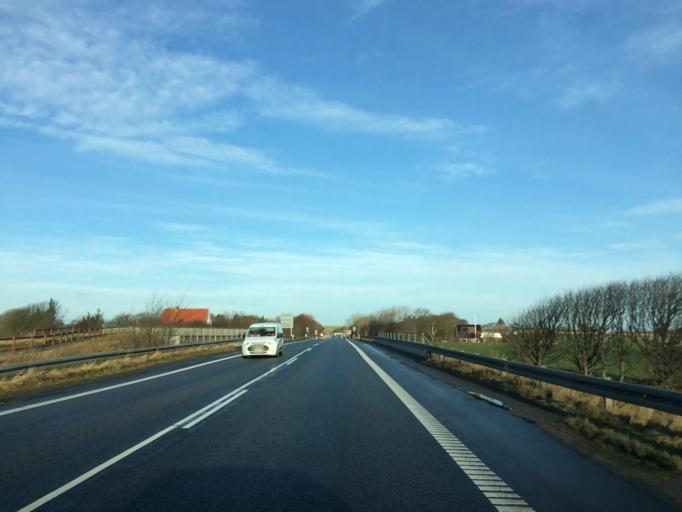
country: DK
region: Central Jutland
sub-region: Struer Kommune
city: Struer
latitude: 56.5133
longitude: 8.5694
